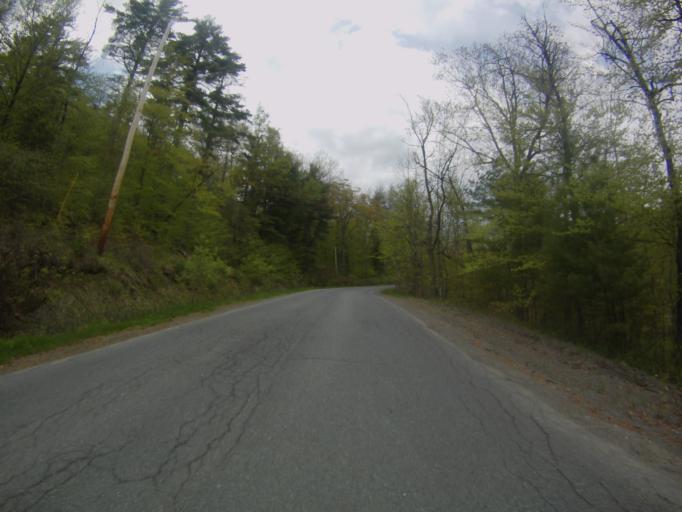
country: US
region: New York
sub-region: Essex County
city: Ticonderoga
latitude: 43.8851
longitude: -73.4810
